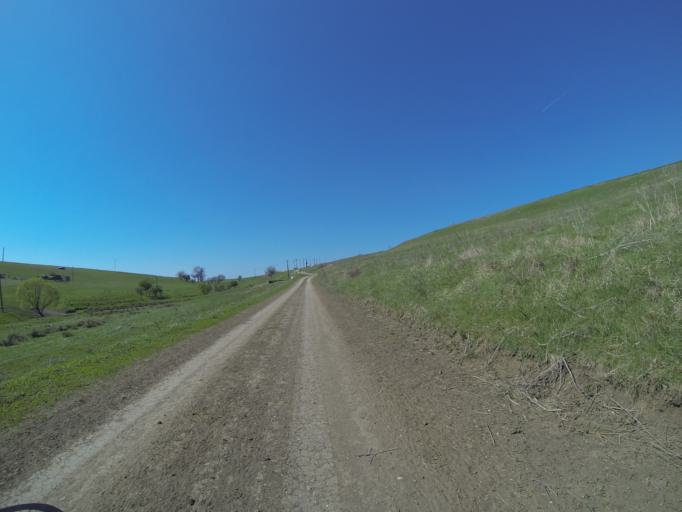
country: RO
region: Dolj
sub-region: Comuna Caloparu
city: Salcuta
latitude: 44.1582
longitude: 23.6696
